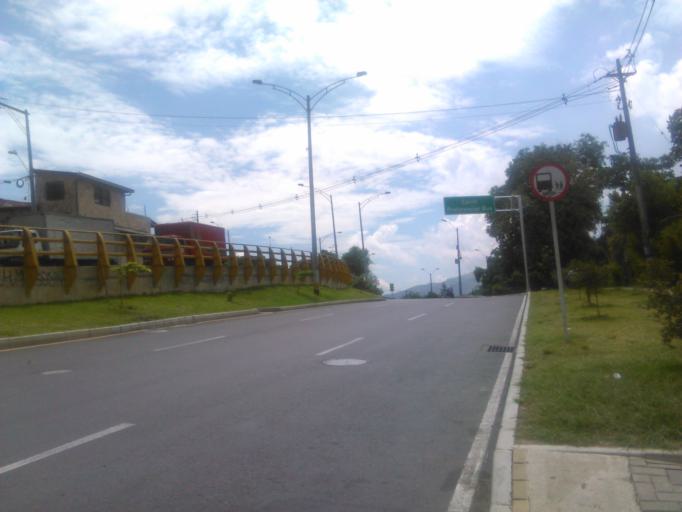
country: CO
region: Antioquia
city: Medellin
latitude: 6.2827
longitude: -75.5846
